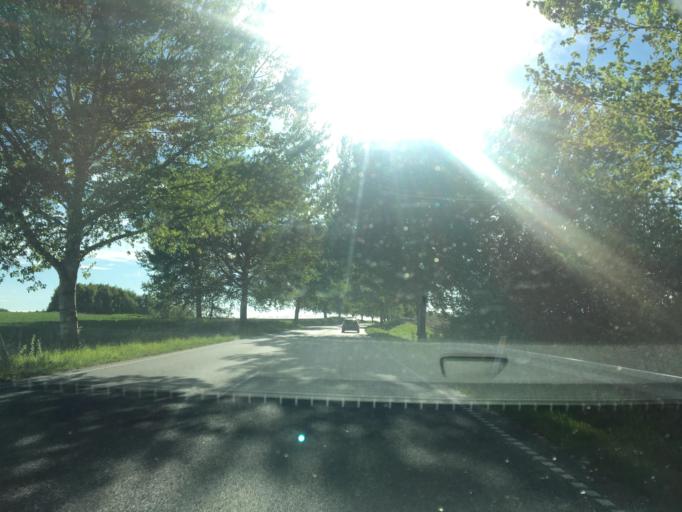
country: DK
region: Capital Region
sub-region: Frederikssund Kommune
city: Slangerup
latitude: 55.8349
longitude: 12.1807
